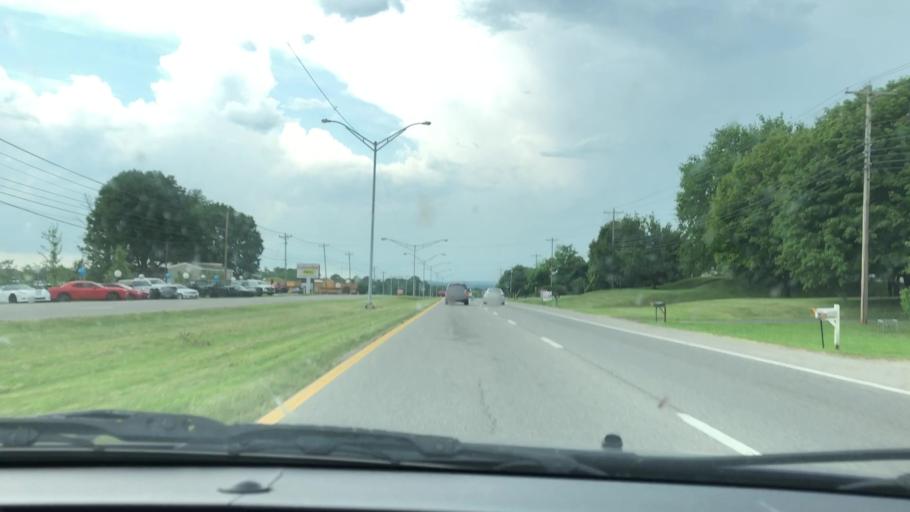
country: US
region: Tennessee
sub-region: Maury County
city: Columbia
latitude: 35.6446
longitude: -87.0135
